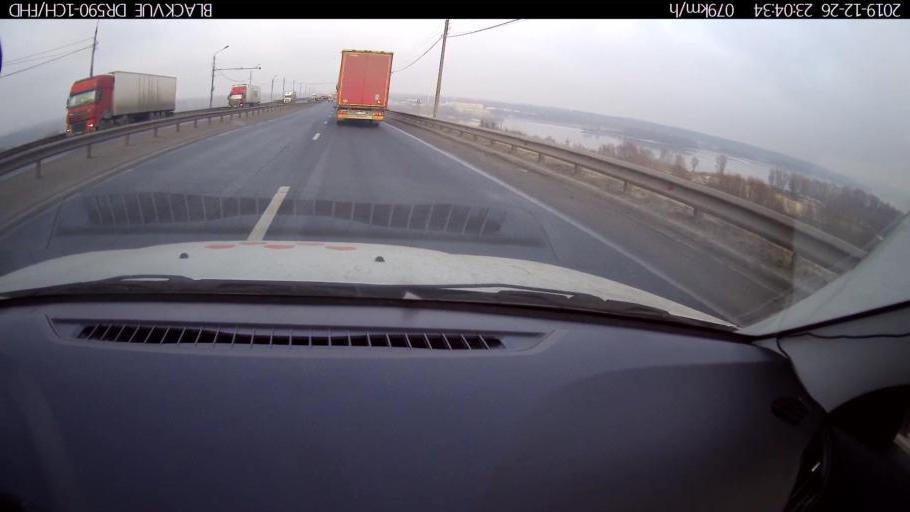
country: RU
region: Nizjnij Novgorod
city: Burevestnik
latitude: 56.1815
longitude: 43.7483
